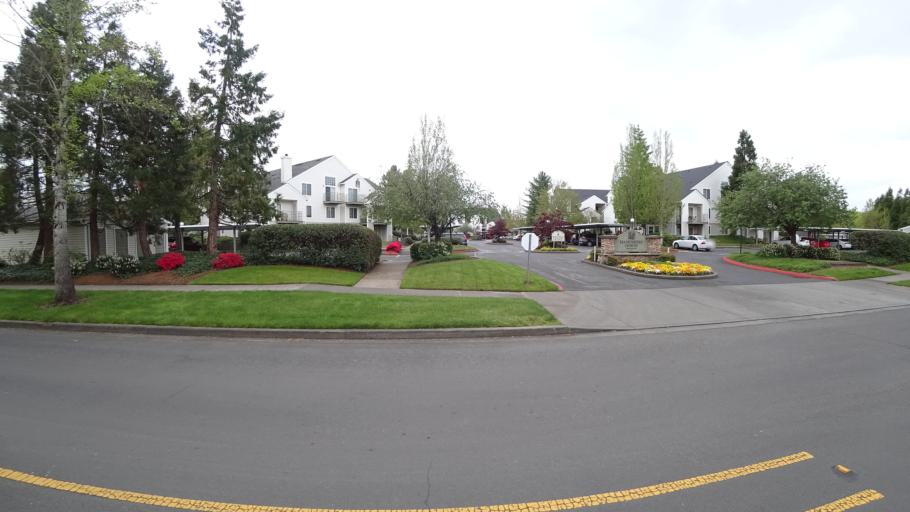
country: US
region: Oregon
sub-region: Washington County
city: Hillsboro
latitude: 45.5454
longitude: -122.9680
